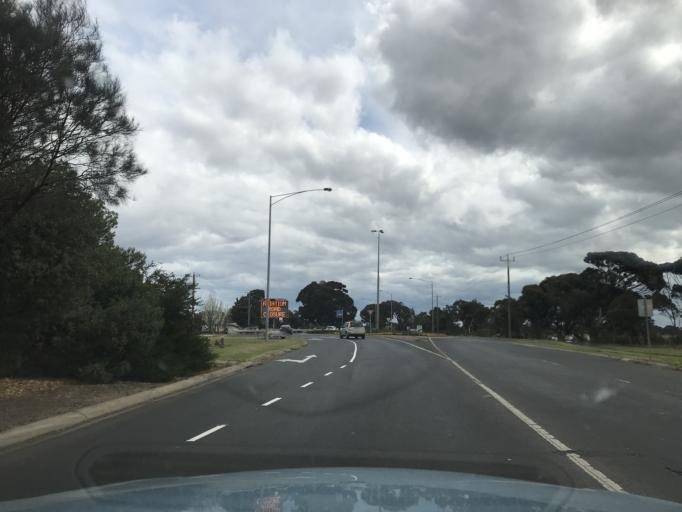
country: AU
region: Victoria
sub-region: Hobsons Bay
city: Laverton
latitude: -37.8481
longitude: 144.7740
